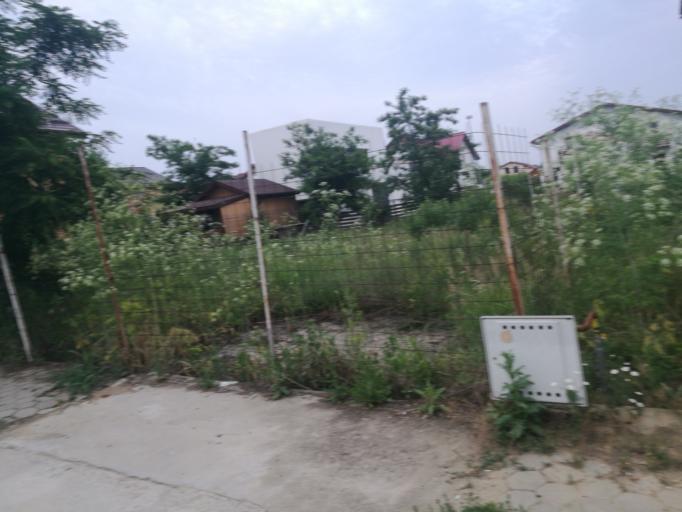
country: RO
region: Ilfov
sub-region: Comuna Vidra
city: Vidra
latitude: 44.2772
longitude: 26.1806
